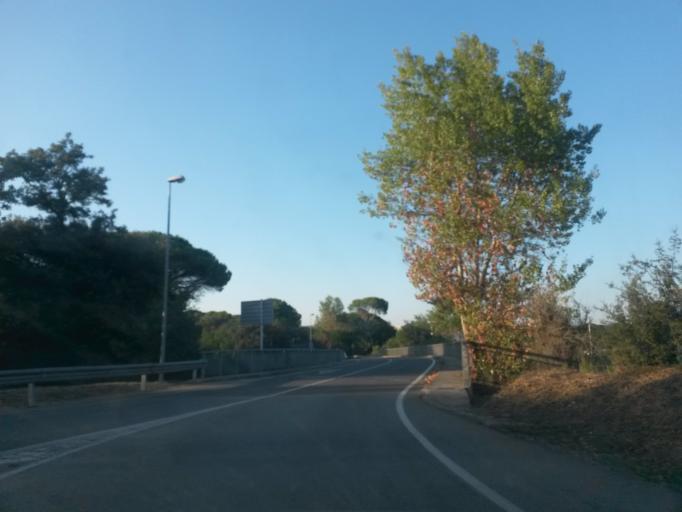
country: ES
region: Catalonia
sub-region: Provincia de Girona
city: Fornells de la Selva
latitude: 41.9468
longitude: 2.8140
